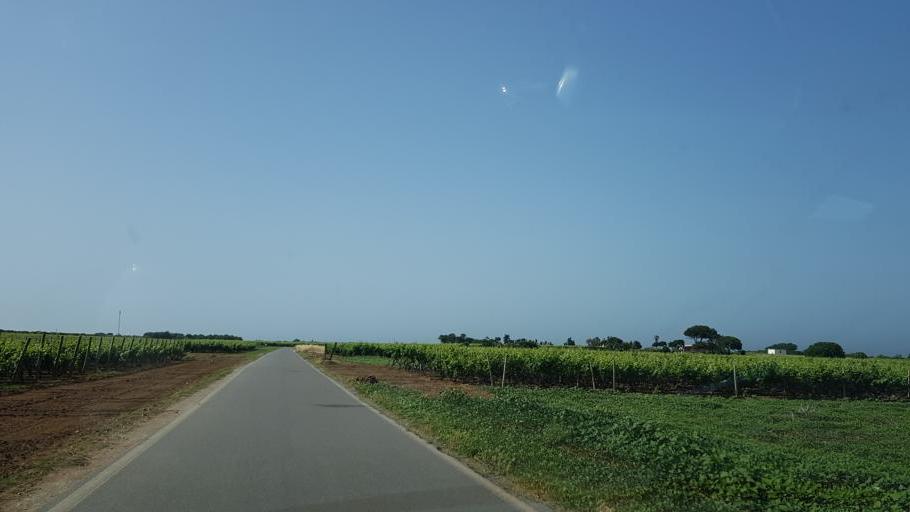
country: IT
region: Apulia
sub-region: Provincia di Brindisi
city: Brindisi
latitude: 40.6739
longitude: 17.8869
